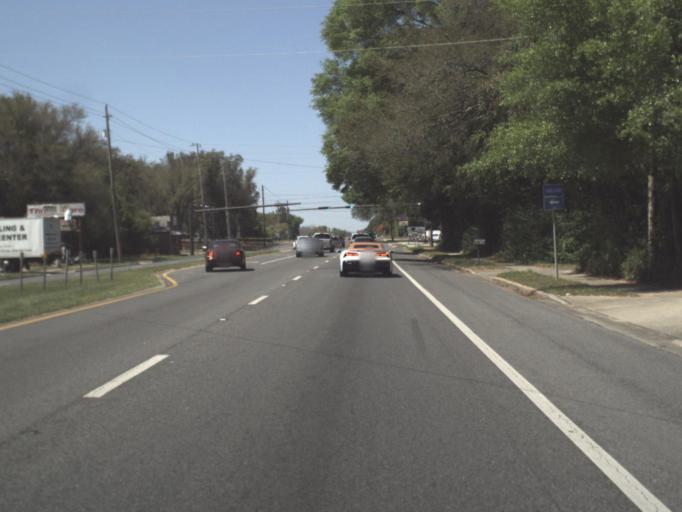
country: US
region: Florida
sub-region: Escambia County
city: Bellview
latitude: 30.4673
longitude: -87.3039
